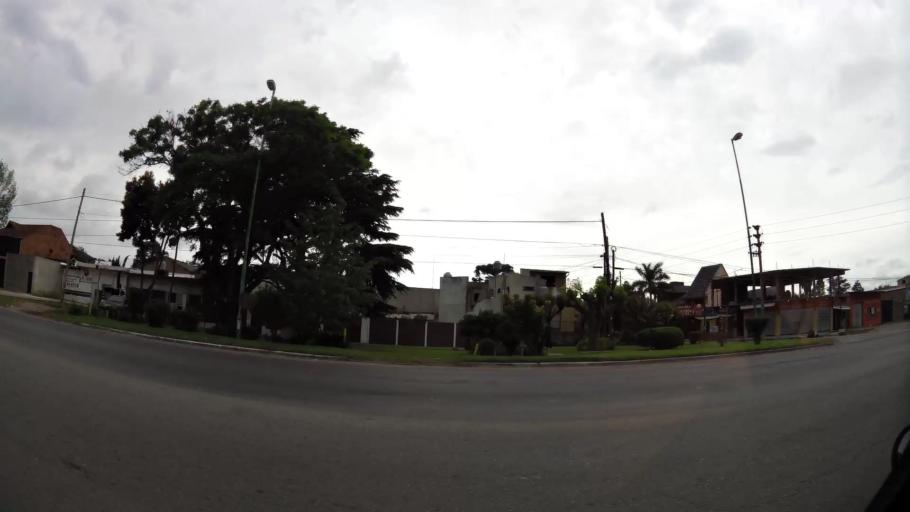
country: AR
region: Buenos Aires
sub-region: Partido de Quilmes
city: Quilmes
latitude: -34.7758
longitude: -58.2811
